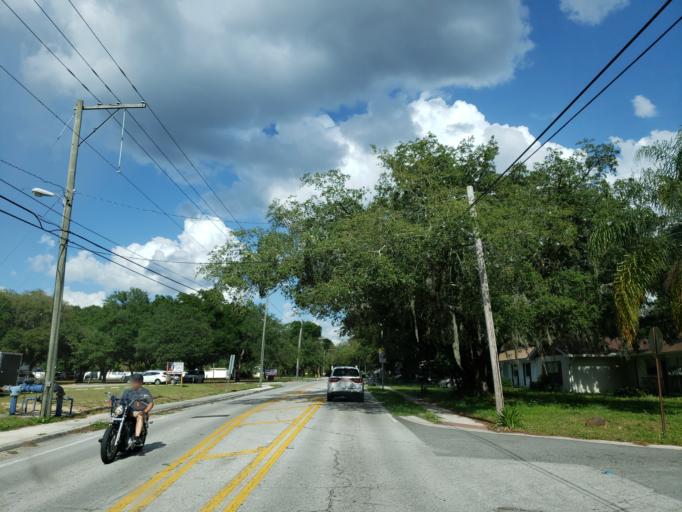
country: US
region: Florida
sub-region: Hillsborough County
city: Brandon
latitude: 27.9596
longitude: -82.2835
